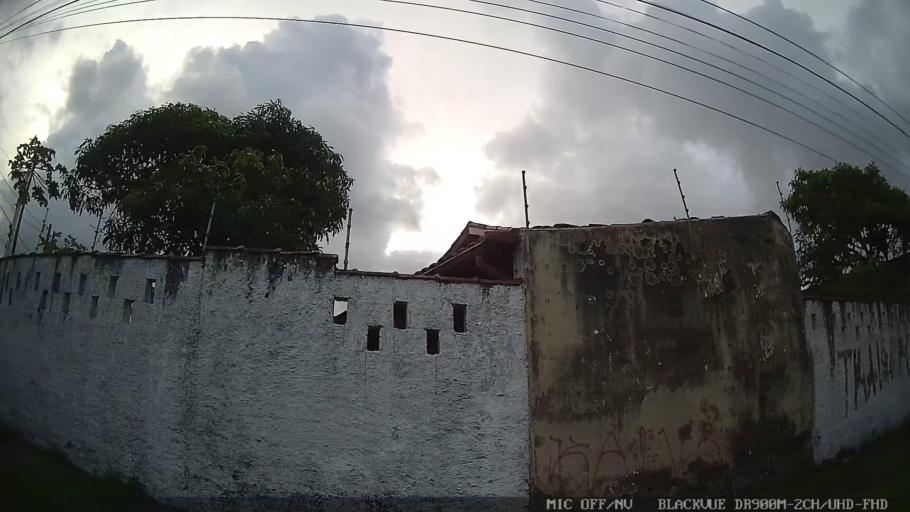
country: BR
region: Sao Paulo
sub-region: Itanhaem
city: Itanhaem
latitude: -24.1504
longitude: -46.7289
